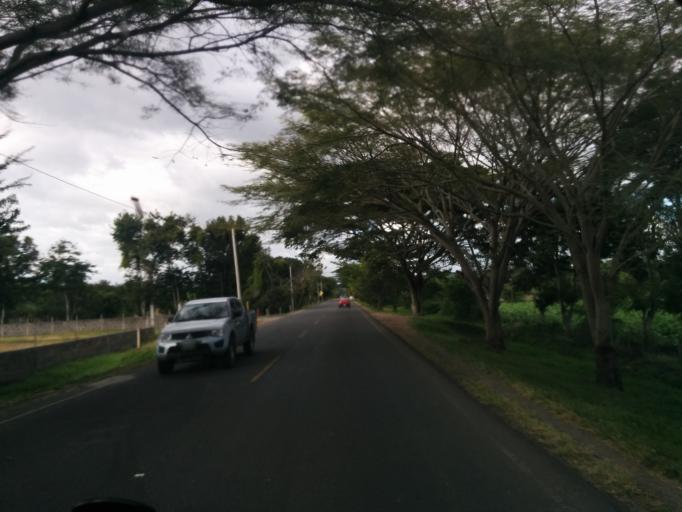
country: NI
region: Esteli
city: Esteli
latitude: 13.1290
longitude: -86.3645
